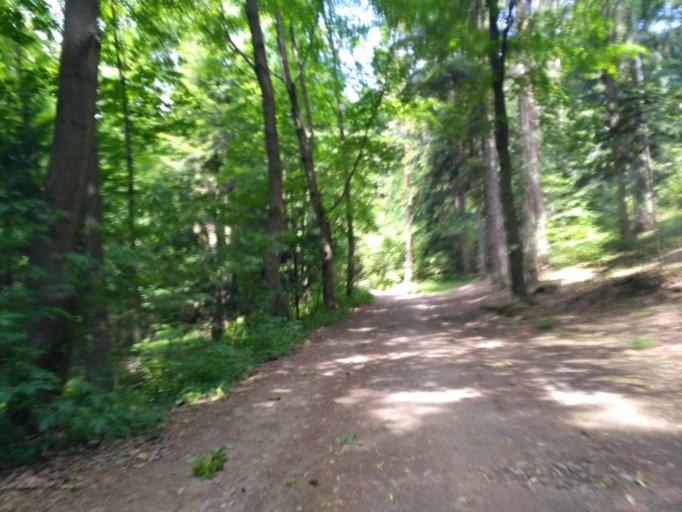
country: PL
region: Subcarpathian Voivodeship
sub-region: Powiat jasielski
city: Brzyska
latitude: 49.8065
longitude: 21.3647
